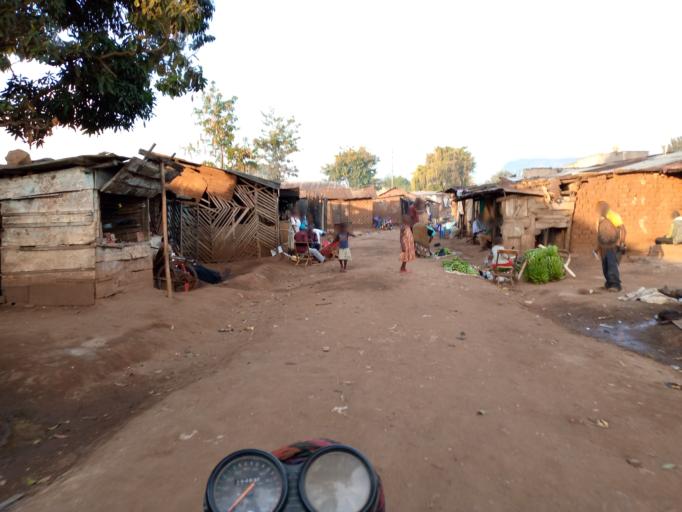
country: UG
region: Eastern Region
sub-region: Mbale District
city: Mbale
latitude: 1.0802
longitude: 34.1630
